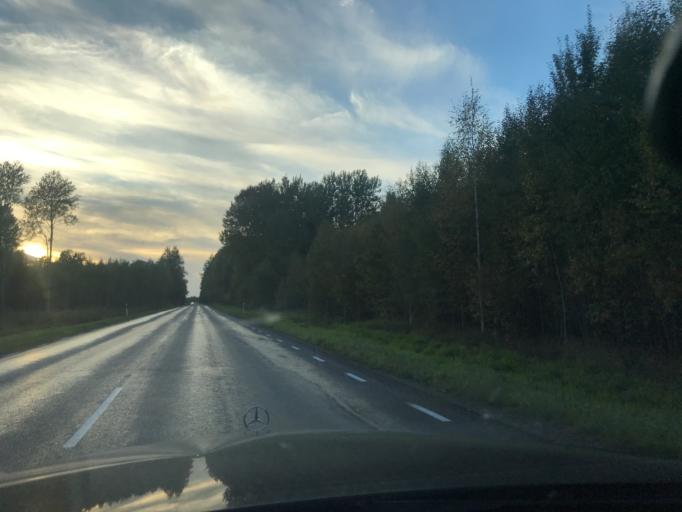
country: EE
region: Vorumaa
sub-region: Antsla vald
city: Vana-Antsla
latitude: 57.9046
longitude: 26.4497
